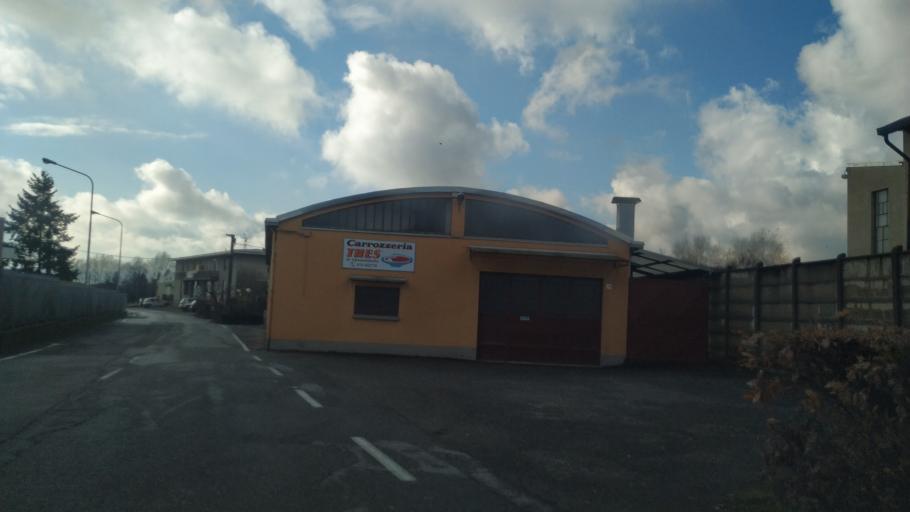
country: IT
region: Piedmont
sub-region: Provincia di Biella
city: Occhieppo Inferiore
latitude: 45.5537
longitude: 8.0391
